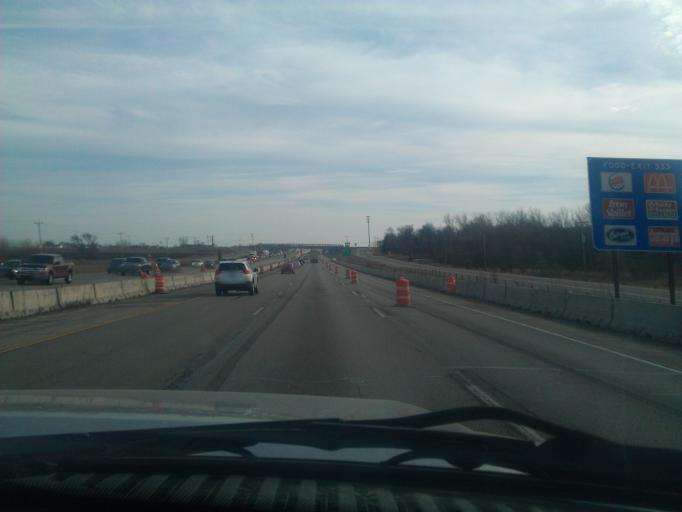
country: US
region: Wisconsin
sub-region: Racine County
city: Franksville
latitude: 42.7401
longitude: -87.9542
